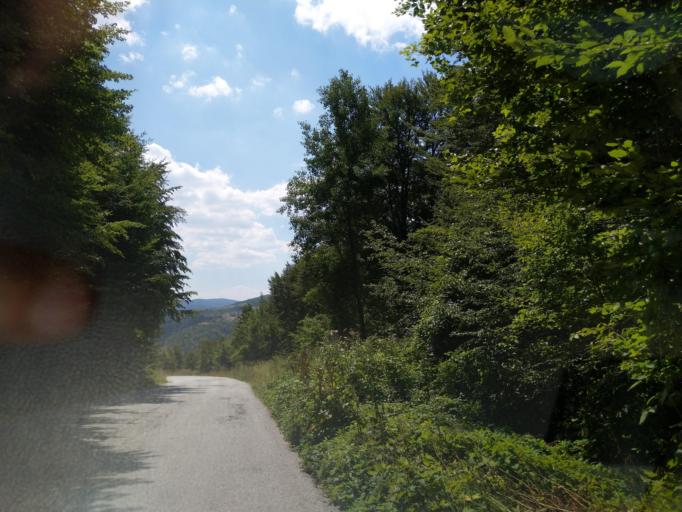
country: RS
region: Central Serbia
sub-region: Zlatiborski Okrug
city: Nova Varos
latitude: 43.4271
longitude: 19.9376
